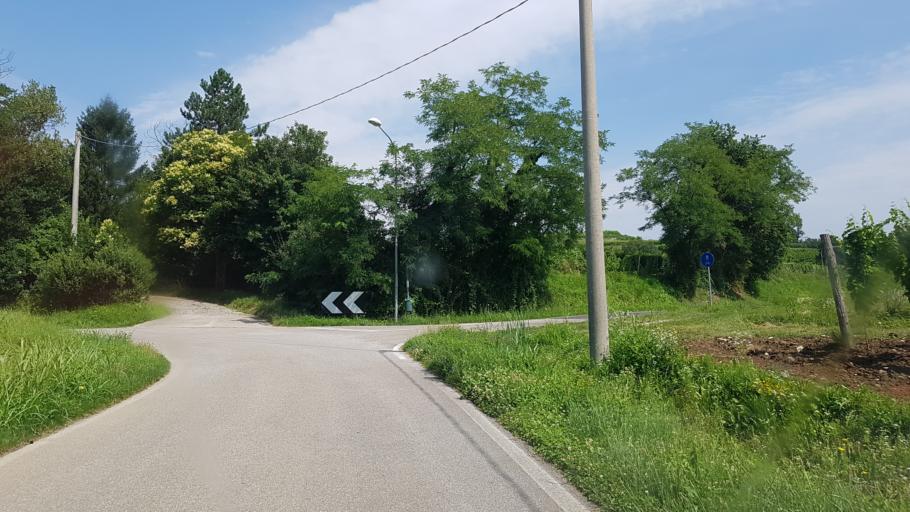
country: IT
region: Friuli Venezia Giulia
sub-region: Provincia di Gorizia
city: Mossa
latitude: 45.9367
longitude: 13.5395
